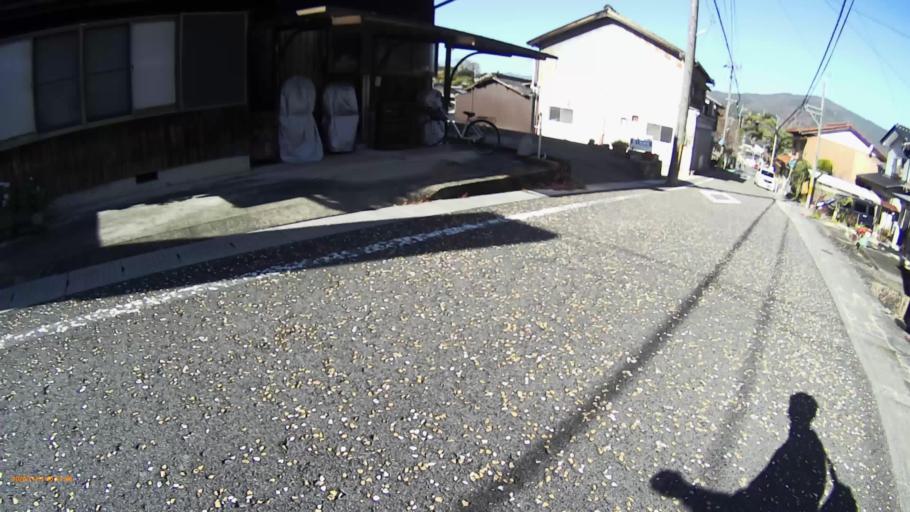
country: JP
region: Gifu
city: Nakatsugawa
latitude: 35.5122
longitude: 137.5306
